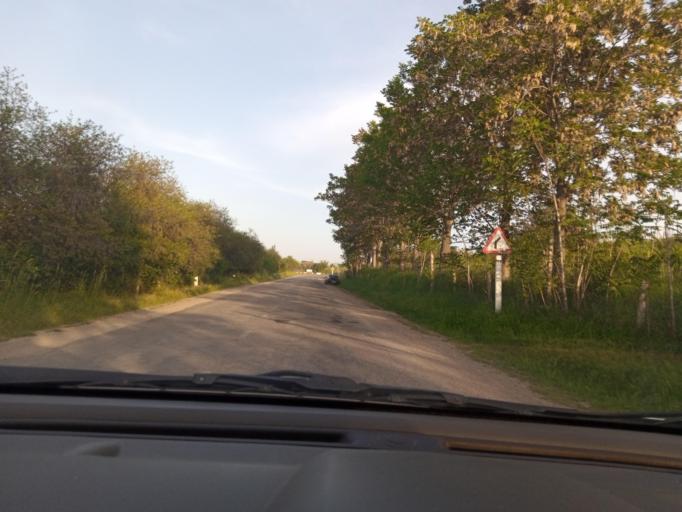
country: UZ
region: Toshkent
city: Parkent
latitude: 41.2368
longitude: 69.7355
